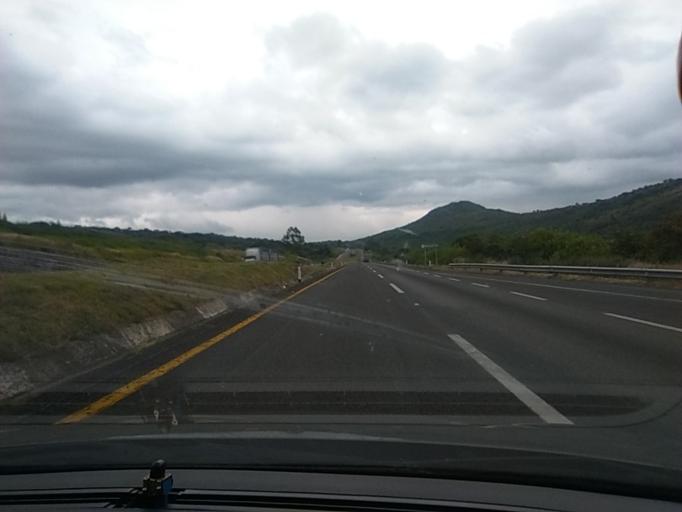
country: MX
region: Jalisco
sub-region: Zapotlan del Rey
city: Zapotlan del Rey
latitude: 20.5251
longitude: -102.9996
